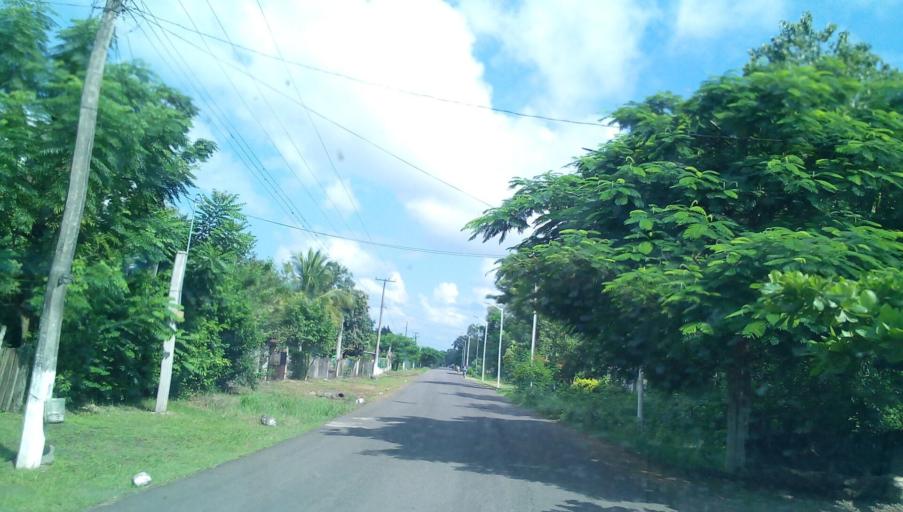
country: MX
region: Veracruz
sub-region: Citlaltepetl
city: Las Sabinas
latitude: 21.3580
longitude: -97.8996
